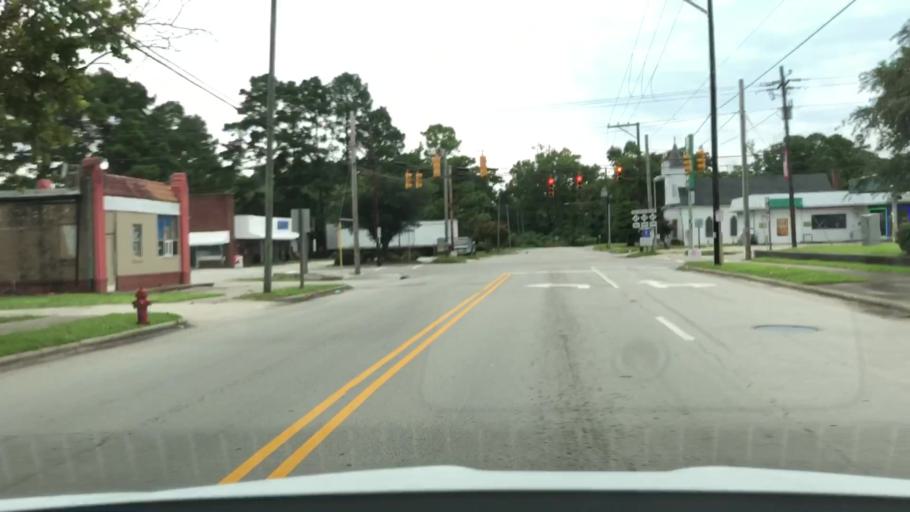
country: US
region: North Carolina
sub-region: Jones County
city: Trenton
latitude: 35.0632
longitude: -77.3538
